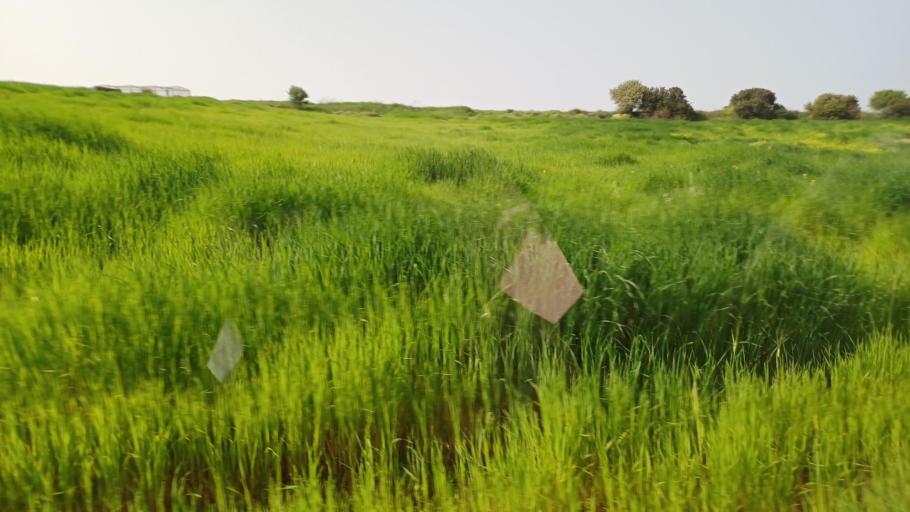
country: CY
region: Pafos
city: Polis
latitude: 35.0082
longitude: 32.3574
